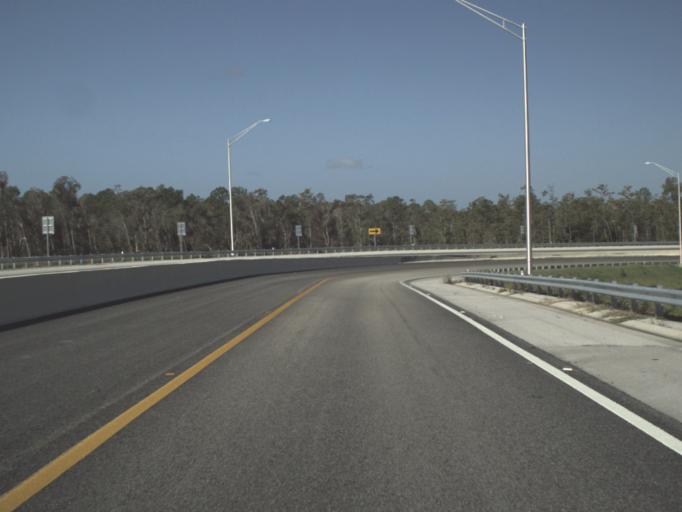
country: US
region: Florida
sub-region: Lee County
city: Three Oaks
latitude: 26.5118
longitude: -81.7958
